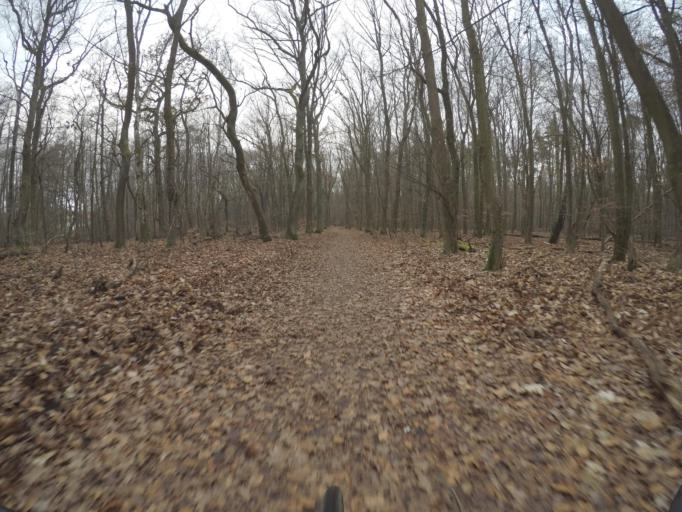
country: DE
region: Berlin
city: Grunau
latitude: 52.4175
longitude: 13.5977
